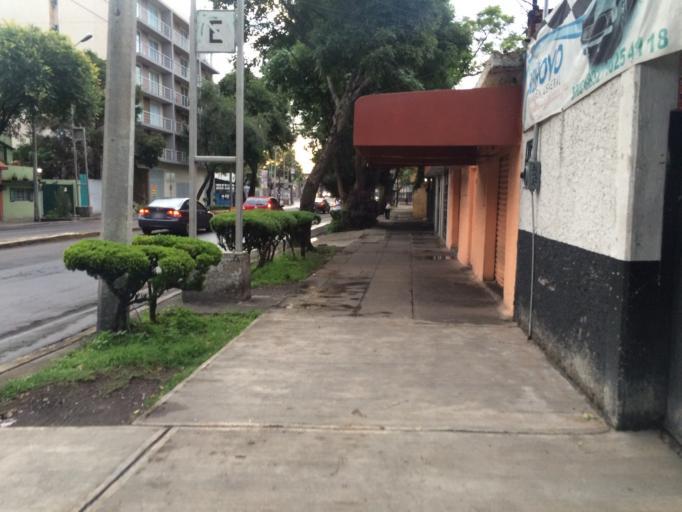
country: MX
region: Mexico City
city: Colonia Nativitas
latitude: 19.3637
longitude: -99.1398
